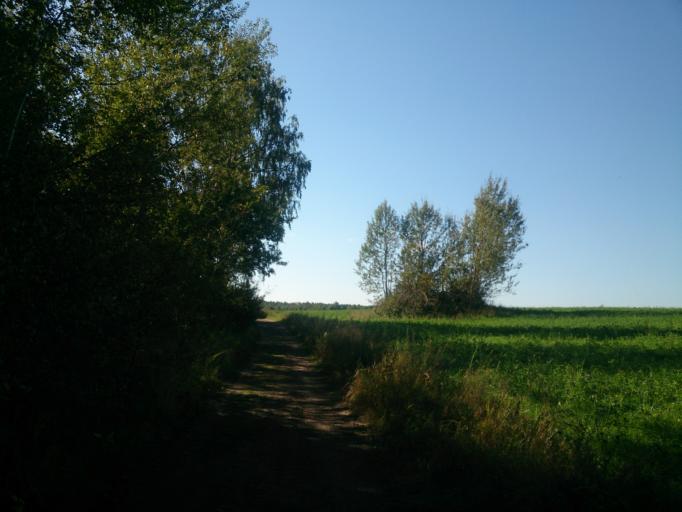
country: SE
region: OEstergoetland
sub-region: Atvidabergs Kommun
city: Atvidaberg
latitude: 58.2235
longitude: 15.9754
